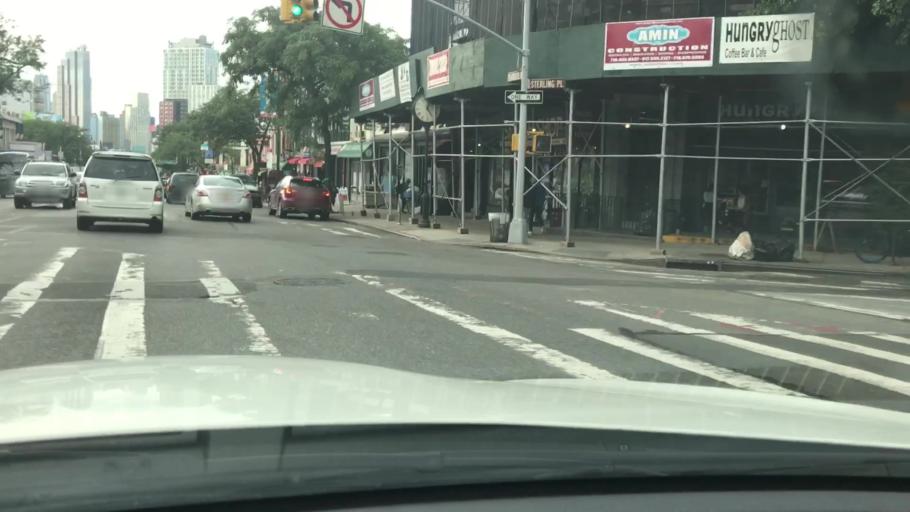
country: US
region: New York
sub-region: Kings County
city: Brooklyn
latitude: 40.6763
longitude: -73.9717
